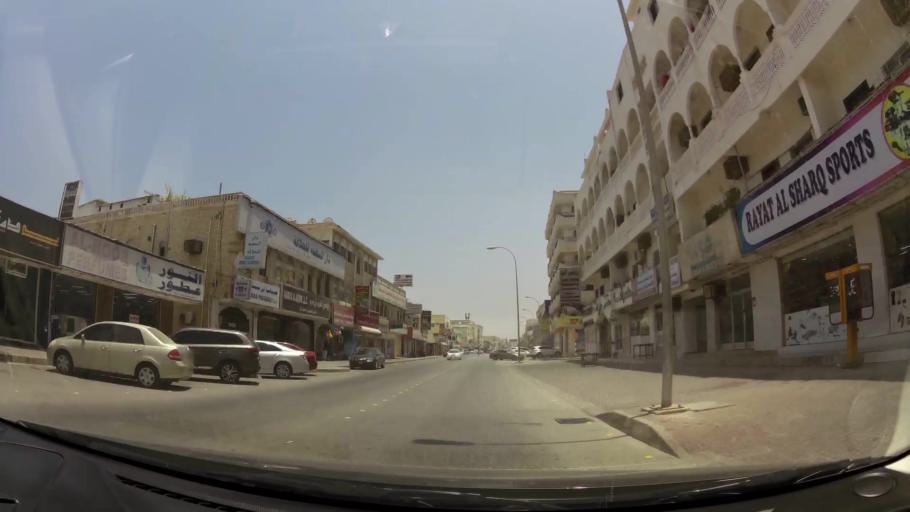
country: OM
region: Zufar
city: Salalah
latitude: 17.0144
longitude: 54.1048
